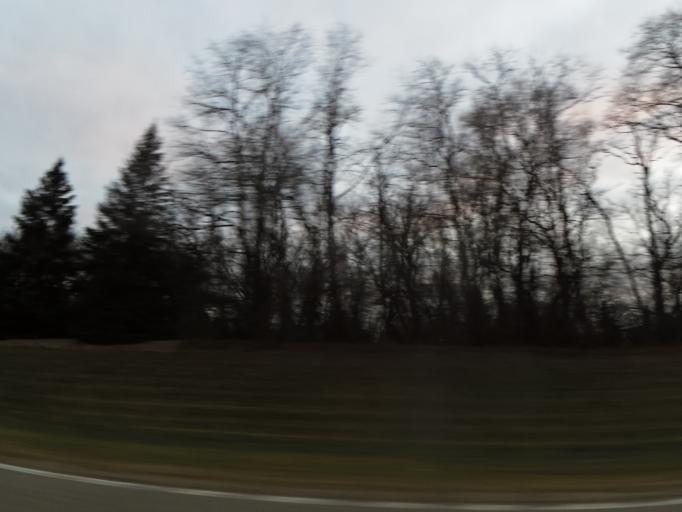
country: US
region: Minnesota
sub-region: Washington County
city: Grant
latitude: 45.0577
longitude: -92.9191
